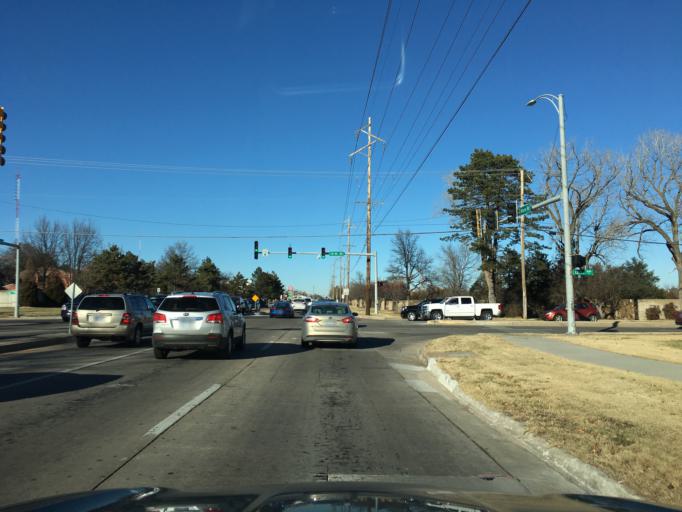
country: US
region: Kansas
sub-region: Sedgwick County
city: Bellaire
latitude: 37.7080
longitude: -97.2446
